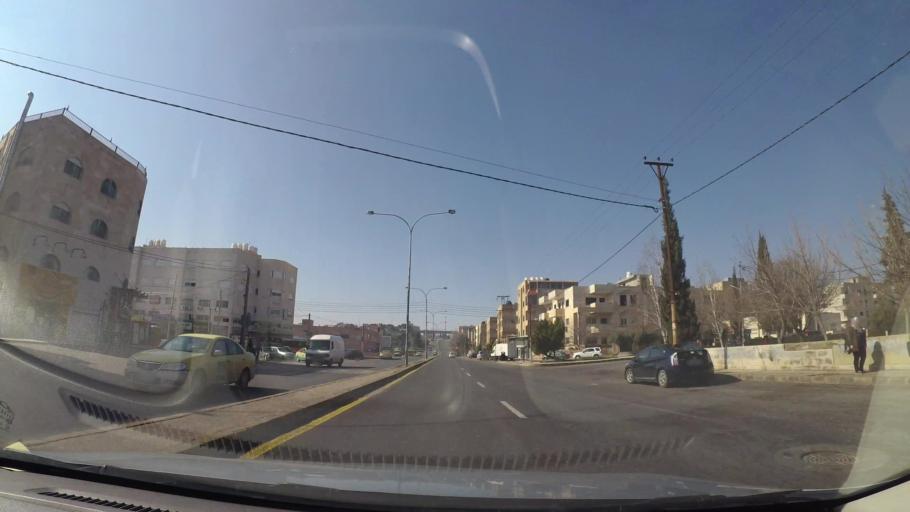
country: JO
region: Amman
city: Al Bunayyat ash Shamaliyah
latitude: 31.9239
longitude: 35.8978
